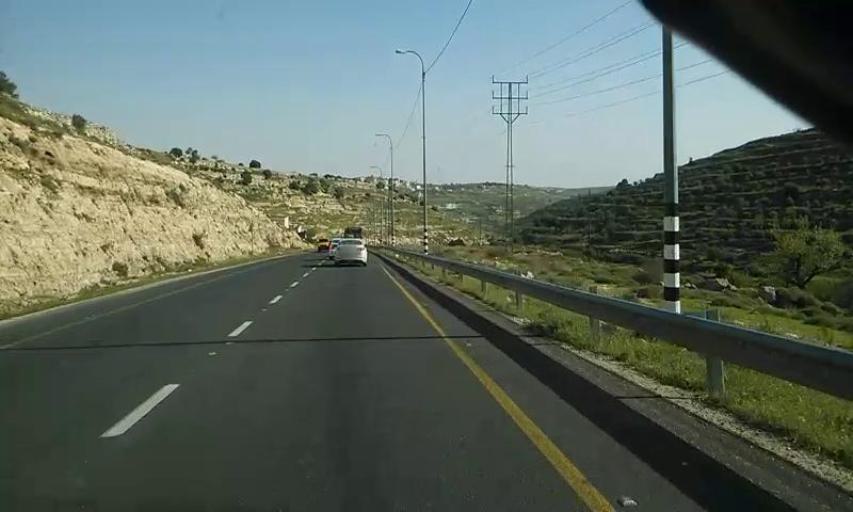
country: PS
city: Al Buq`ah
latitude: 31.5233
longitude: 35.1315
